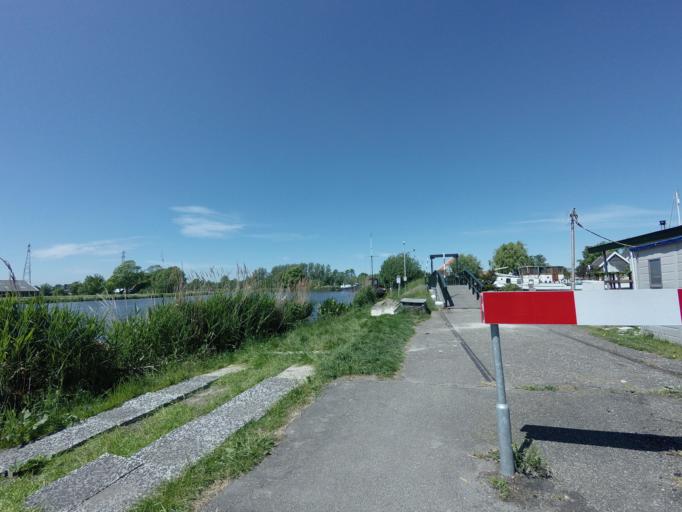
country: NL
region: North Holland
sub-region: Gemeente Uitgeest
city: Uitgeest
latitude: 52.5553
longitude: 4.7936
